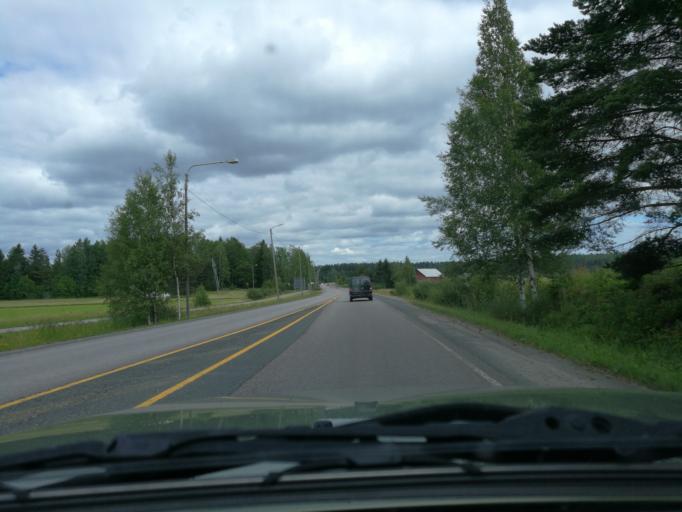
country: FI
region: Uusimaa
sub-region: Helsinki
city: Vantaa
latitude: 60.3147
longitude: 25.0747
